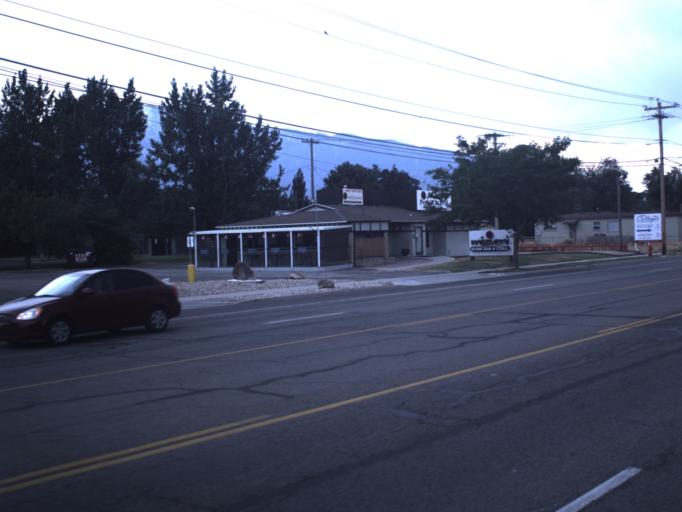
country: US
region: Utah
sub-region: Salt Lake County
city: Sandy City
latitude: 40.5993
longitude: -111.8723
